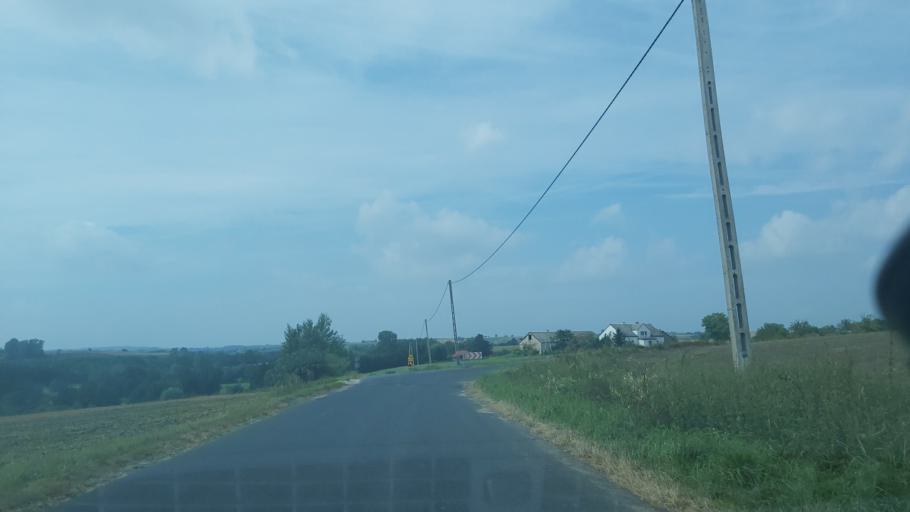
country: PL
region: Kujawsko-Pomorskie
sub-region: Powiat golubsko-dobrzynski
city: Zbojno
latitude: 53.0404
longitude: 19.1675
